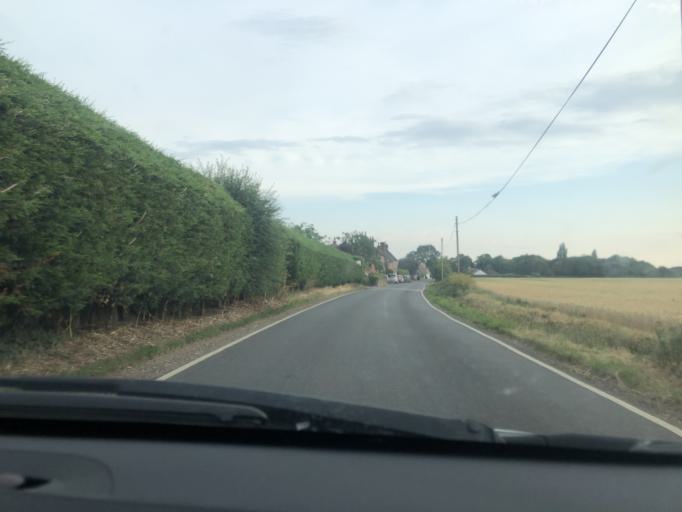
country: GB
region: England
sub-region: Kent
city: Herne Bay
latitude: 51.3433
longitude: 1.1625
